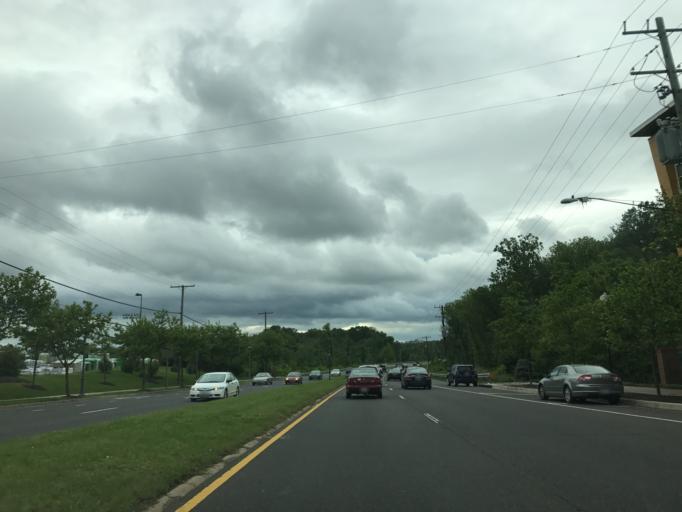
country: US
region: Maryland
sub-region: Prince George's County
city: Hyattsville
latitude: 38.9672
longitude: -76.9647
